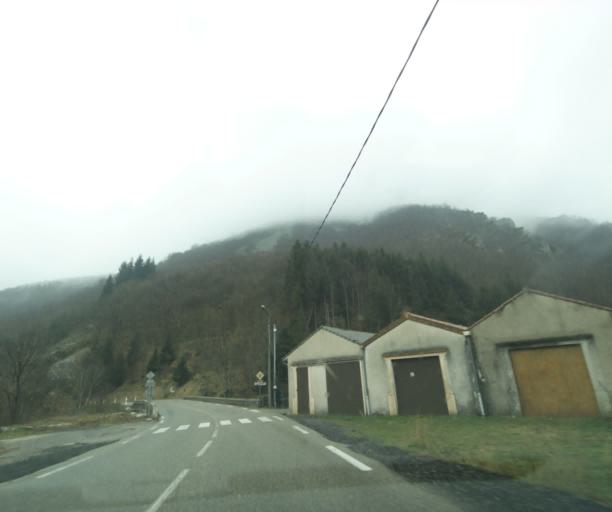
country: FR
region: Rhone-Alpes
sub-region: Departement de l'Ardeche
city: Thueyts
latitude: 44.6649
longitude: 4.1229
